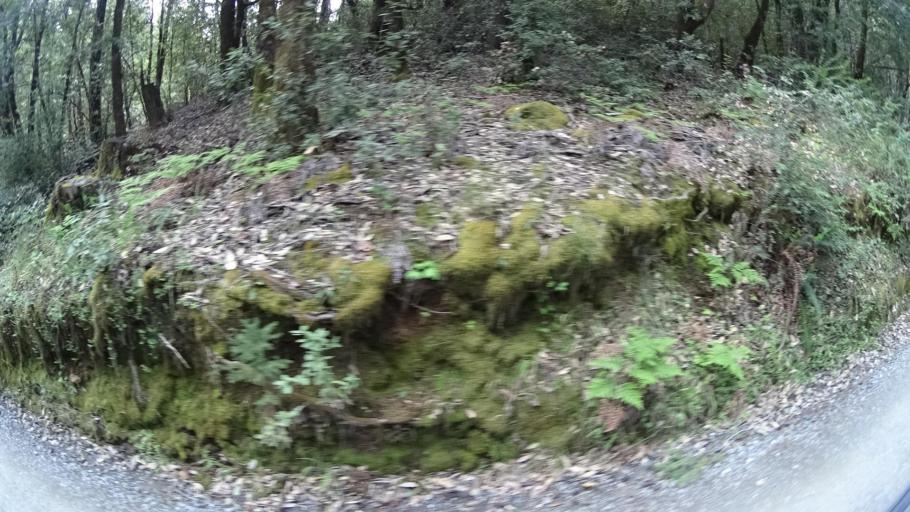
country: US
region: California
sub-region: Humboldt County
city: Redway
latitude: 40.0482
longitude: -123.8369
